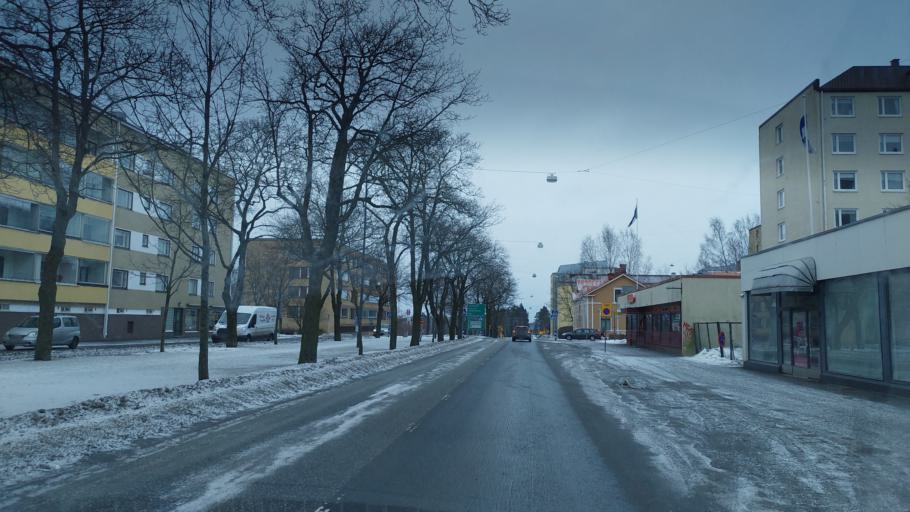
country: FI
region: Ostrobothnia
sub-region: Vaasa
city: Vaasa
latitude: 63.0898
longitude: 21.6210
